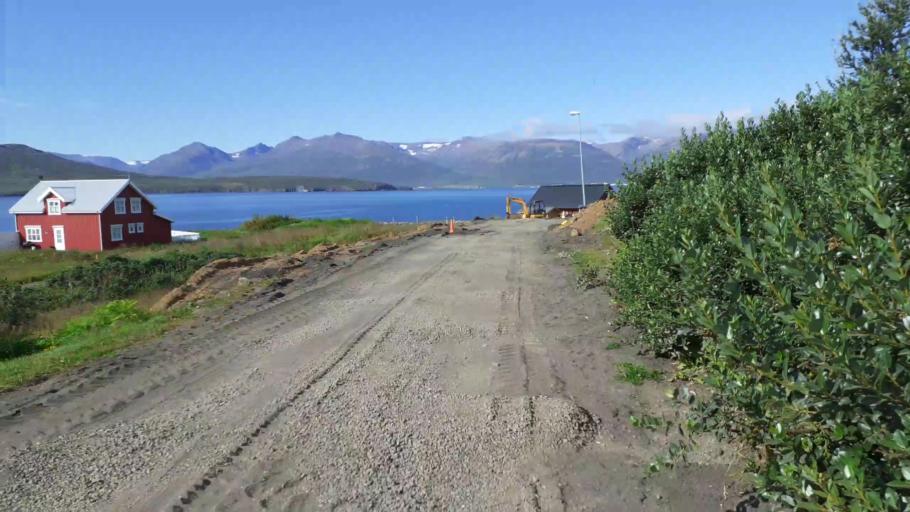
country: IS
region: Northeast
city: Dalvik
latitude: 65.9779
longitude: -18.3668
